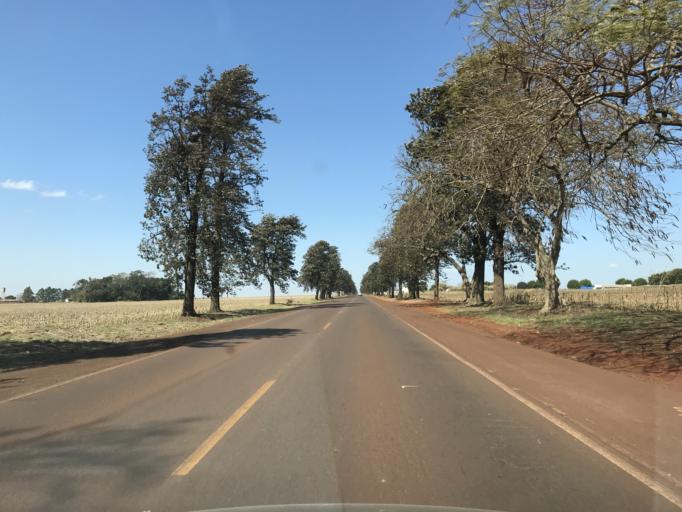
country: BR
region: Parana
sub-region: Palotina
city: Palotina
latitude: -24.4474
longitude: -53.8357
